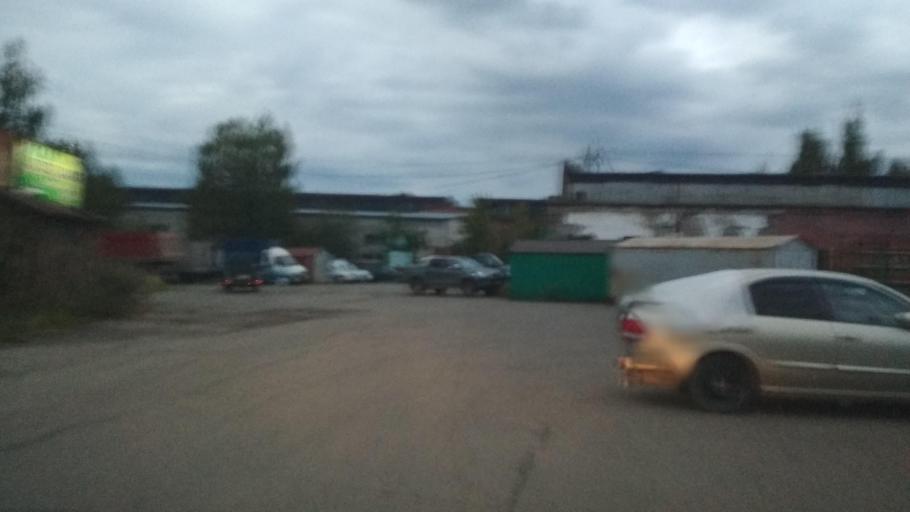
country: RU
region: Tomsk
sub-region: Tomskiy Rayon
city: Tomsk
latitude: 56.4787
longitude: 85.0185
